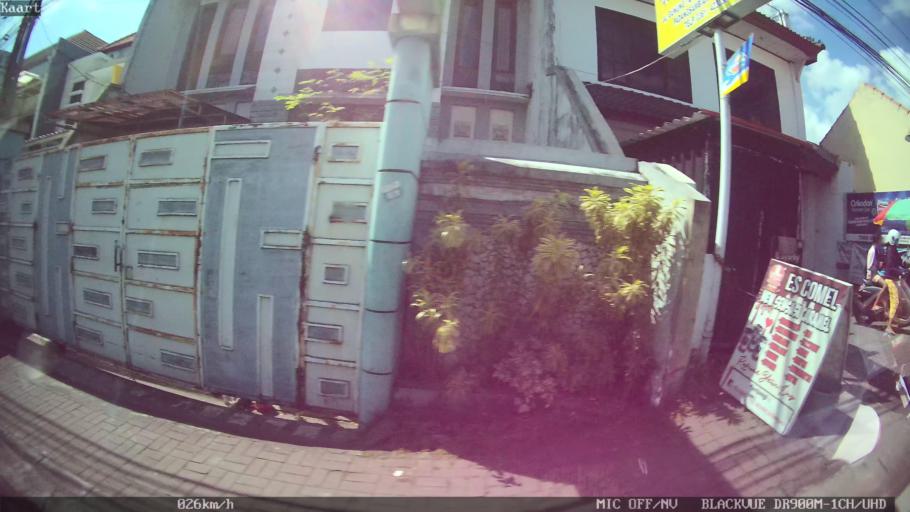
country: ID
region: Bali
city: Denpasar
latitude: -8.6577
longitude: 115.1840
